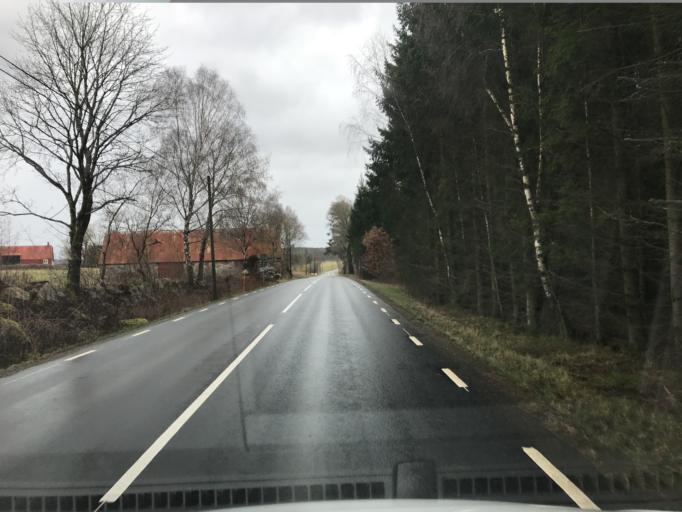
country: SE
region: Skane
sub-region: Perstorps Kommun
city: Perstorp
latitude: 56.0282
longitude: 13.4315
